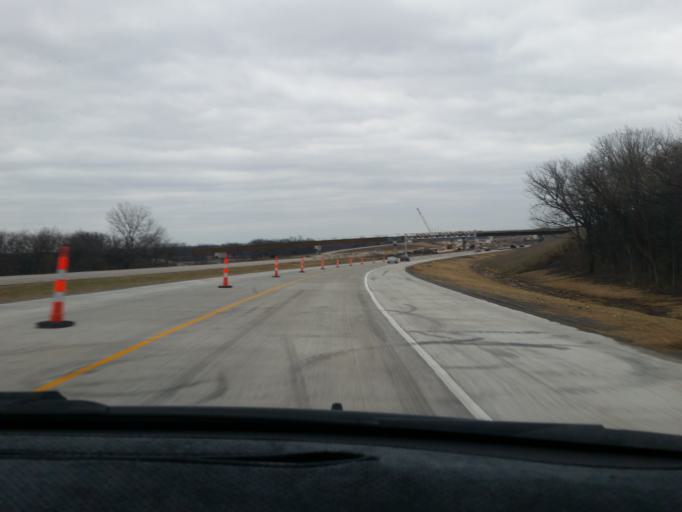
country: US
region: Kansas
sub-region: Douglas County
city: Lawrence
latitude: 38.9413
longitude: -95.1799
